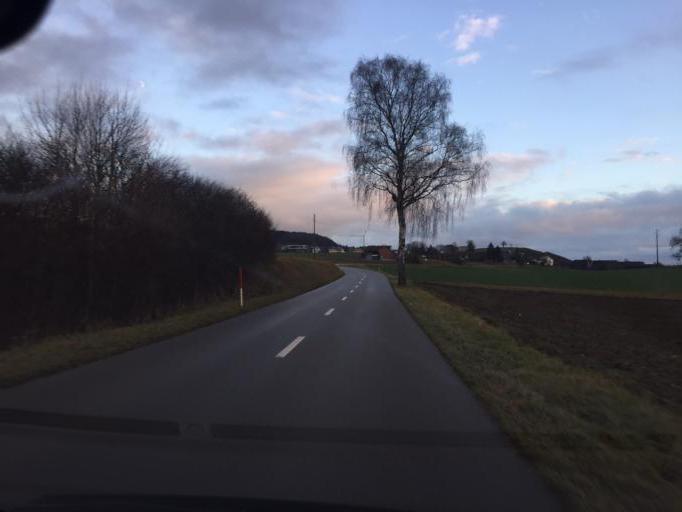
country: DE
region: Baden-Wuerttemberg
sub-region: Freiburg Region
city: Busingen
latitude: 47.7116
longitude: 8.7129
